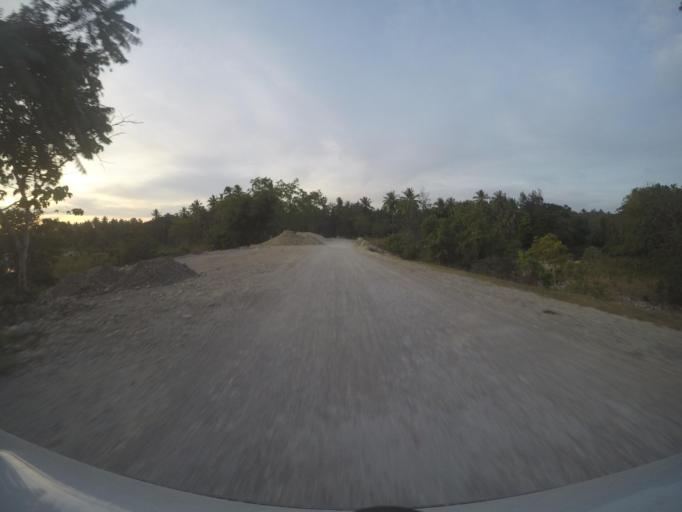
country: TL
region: Viqueque
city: Viqueque
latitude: -8.9008
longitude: 126.3929
